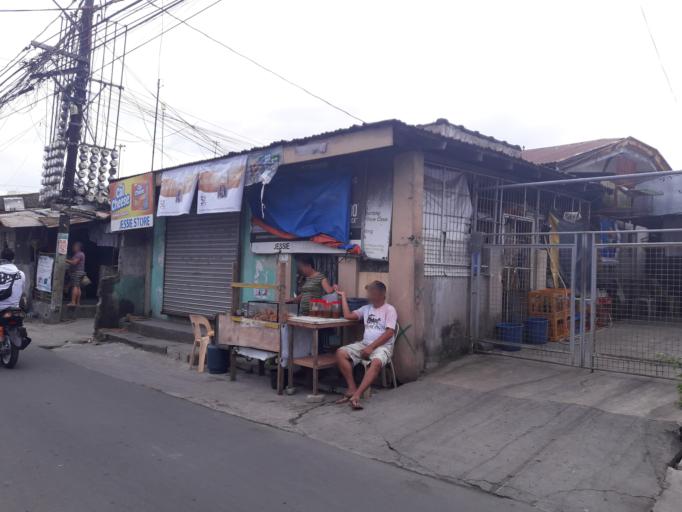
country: PH
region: Calabarzon
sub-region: Province of Laguna
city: Santa Rosa
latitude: 14.3054
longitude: 121.1246
